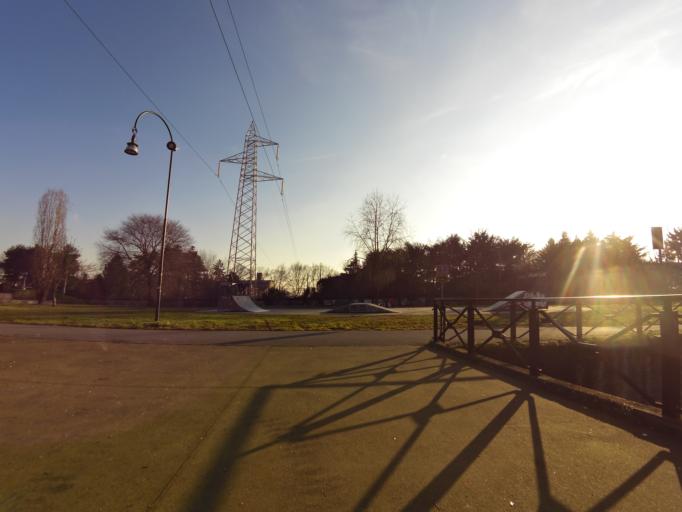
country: IT
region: Lombardy
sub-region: Citta metropolitana di Milano
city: Cologno Monzese
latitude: 45.5170
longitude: 9.2744
